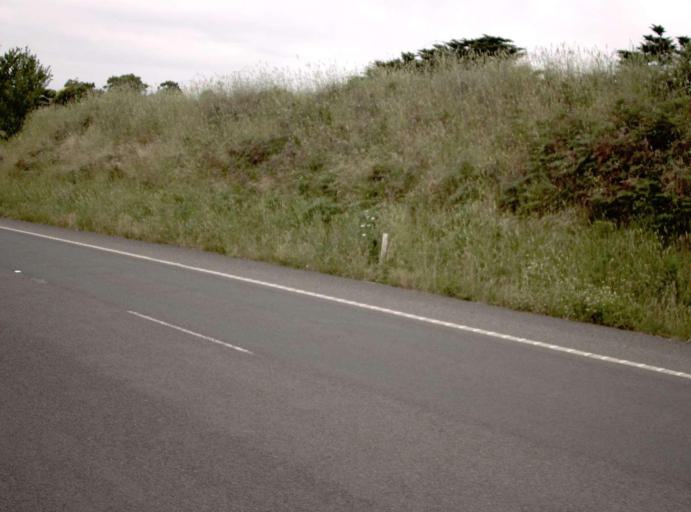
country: AU
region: Victoria
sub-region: Baw Baw
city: Warragul
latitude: -38.4659
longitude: 145.9358
